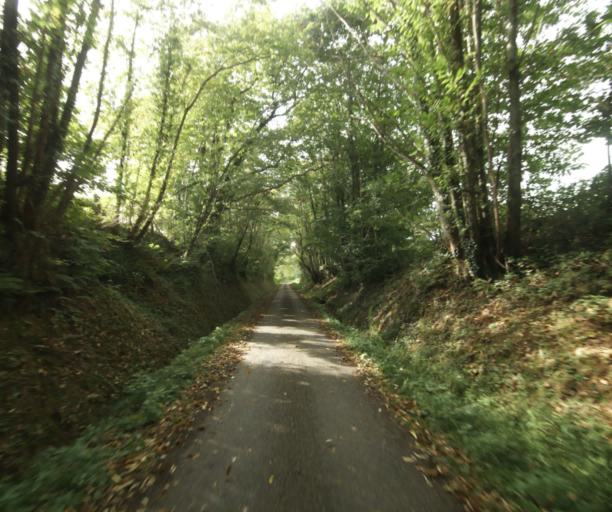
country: FR
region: Midi-Pyrenees
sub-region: Departement du Gers
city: Le Houga
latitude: 43.8788
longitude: -0.1783
